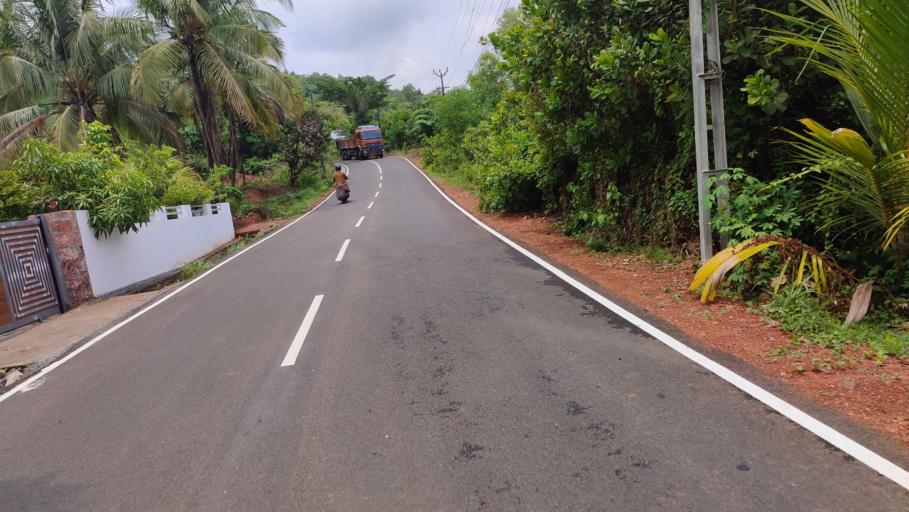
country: IN
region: Kerala
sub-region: Kasaragod District
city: Kannangad
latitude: 12.3154
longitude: 75.1410
